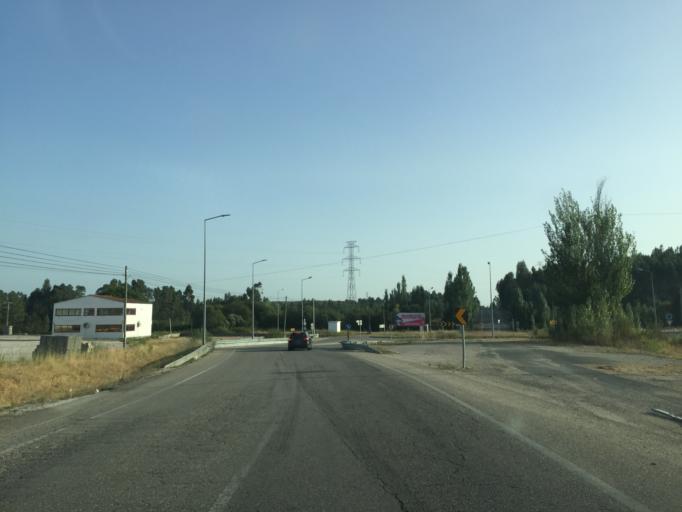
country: PT
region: Santarem
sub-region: Chamusca
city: Vila Nova da Barquinha
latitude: 39.5183
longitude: -8.4122
